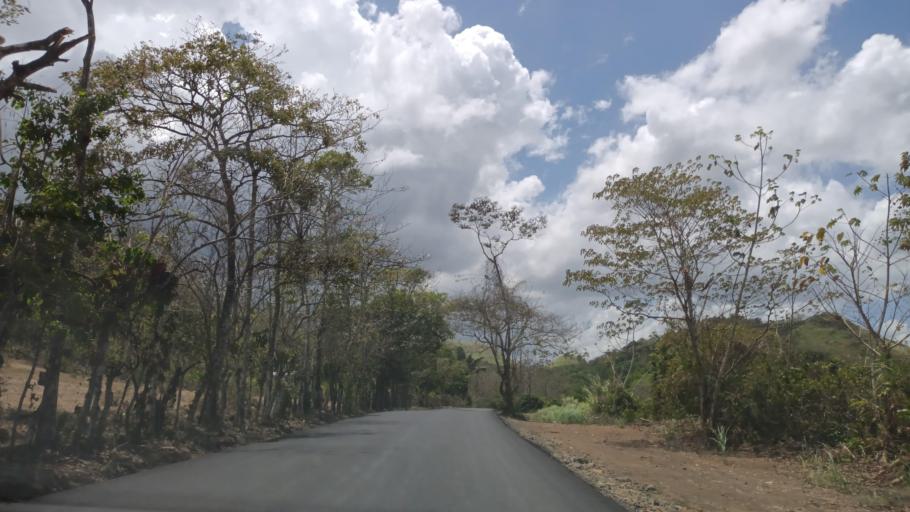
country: PA
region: Panama
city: Alcalde Diaz
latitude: 9.0894
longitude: -79.5772
